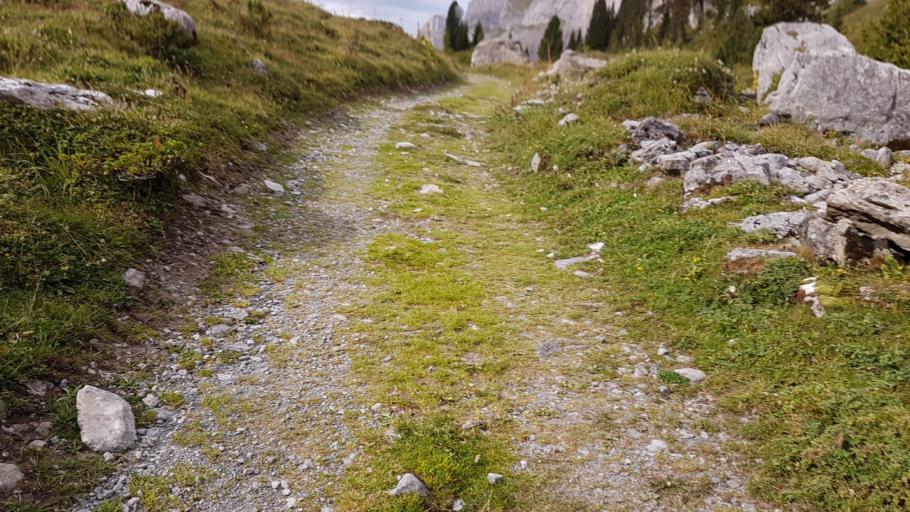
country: CH
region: Bern
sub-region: Frutigen-Niedersimmental District
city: Kandersteg
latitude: 46.4589
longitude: 7.6493
